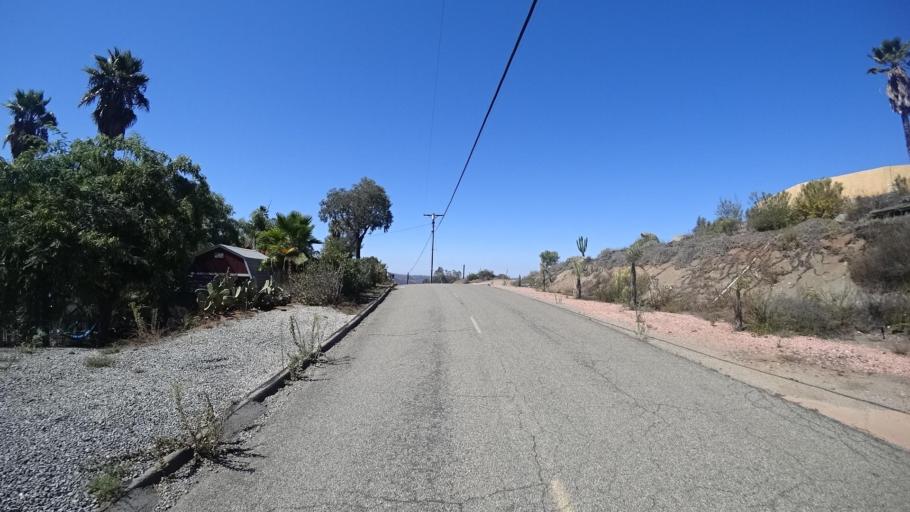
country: US
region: California
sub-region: San Diego County
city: Jamul
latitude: 32.7399
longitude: -116.8762
